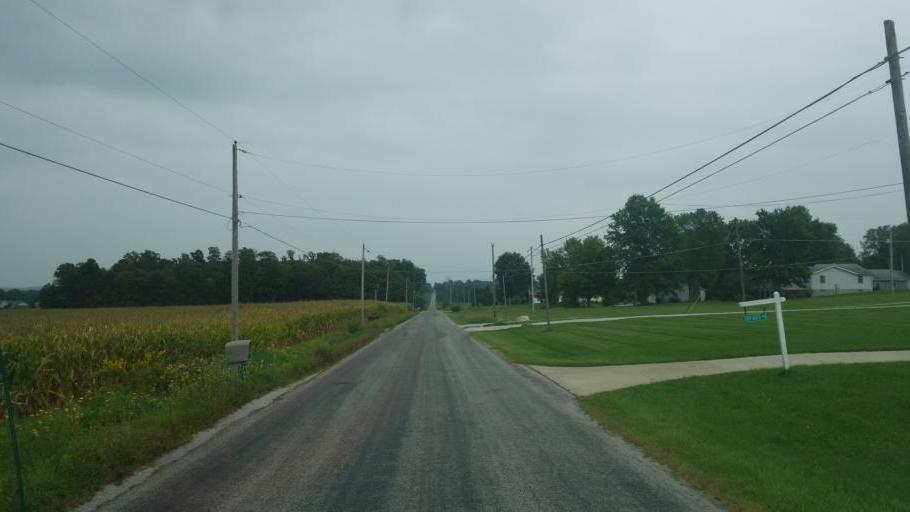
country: US
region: Ohio
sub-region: Wayne County
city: Creston
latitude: 40.9599
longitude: -81.9194
